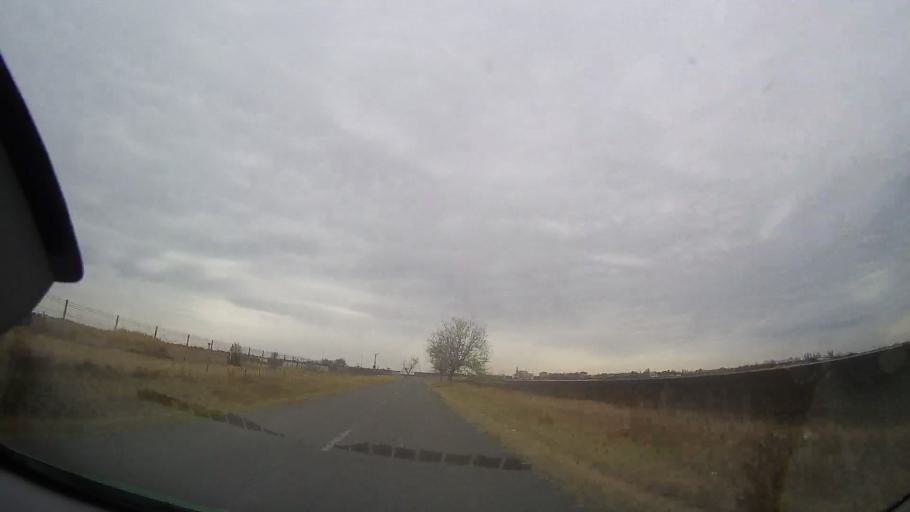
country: RO
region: Prahova
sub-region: Oras Mizil
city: Mizil
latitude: 45.0081
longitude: 26.4211
